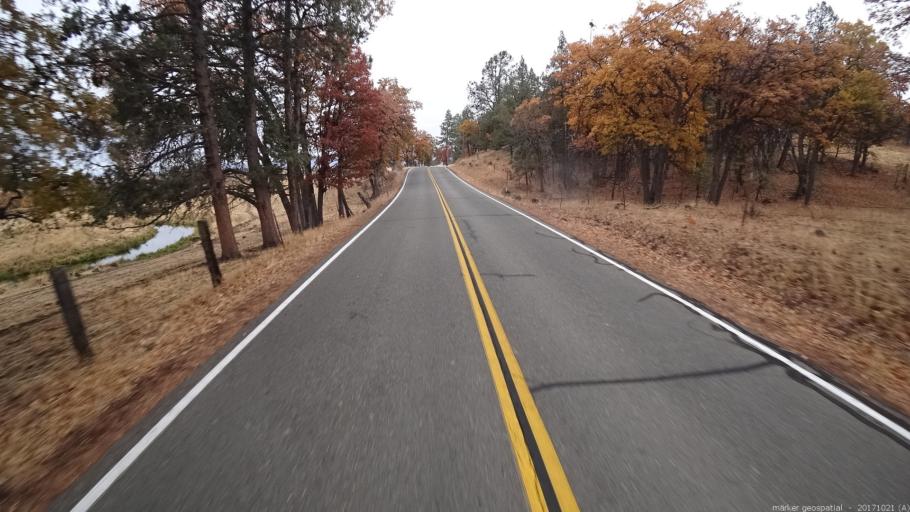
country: US
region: California
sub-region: Shasta County
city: Burney
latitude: 41.0055
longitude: -121.4294
